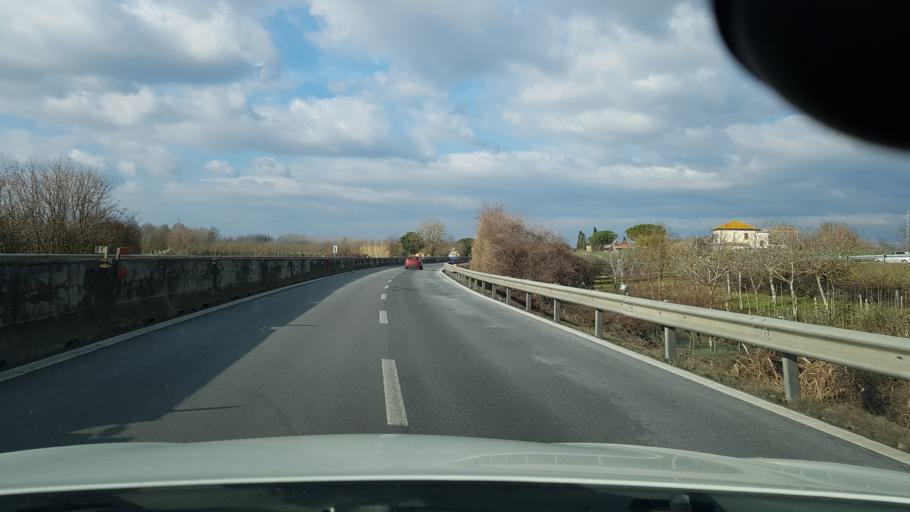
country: IT
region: Tuscany
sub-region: Province of Arezzo
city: Terontola
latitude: 43.1863
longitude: 12.0365
